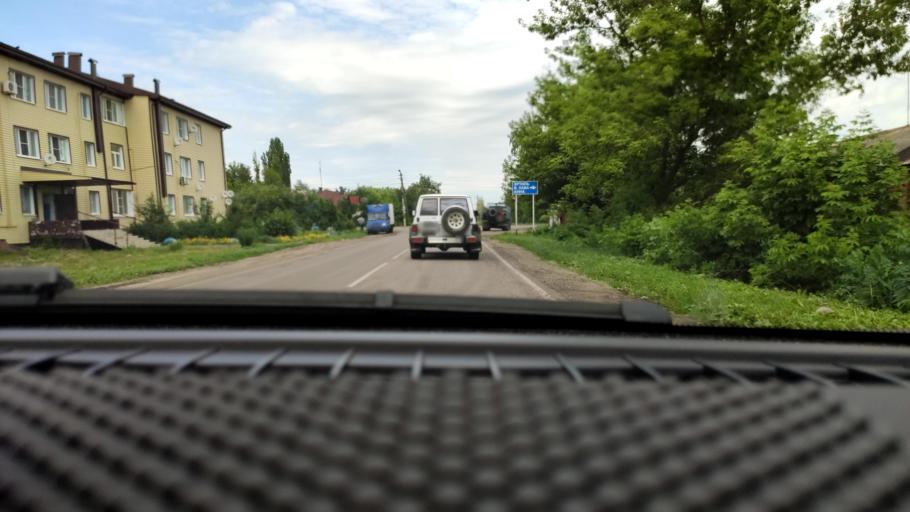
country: RU
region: Voronezj
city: Panino
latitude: 51.6577
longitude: 40.1243
